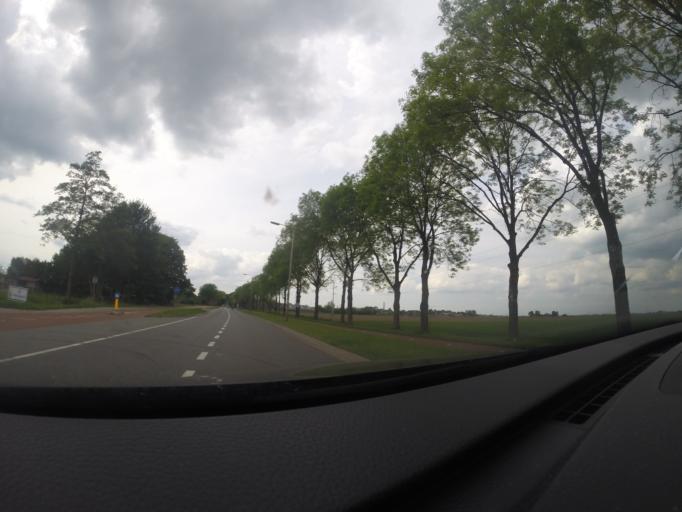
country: NL
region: Gelderland
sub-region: Gemeente Hattem
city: Hattem
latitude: 52.5341
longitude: 6.0229
